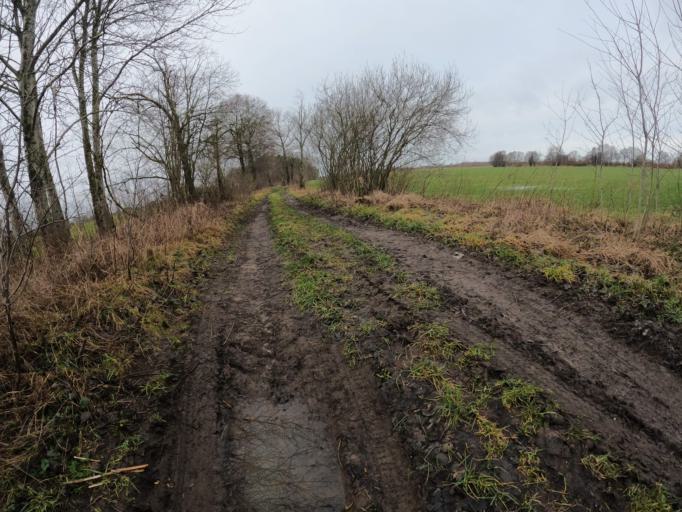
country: PL
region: West Pomeranian Voivodeship
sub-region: Powiat slawienski
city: Darlowo
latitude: 54.4126
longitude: 16.4496
